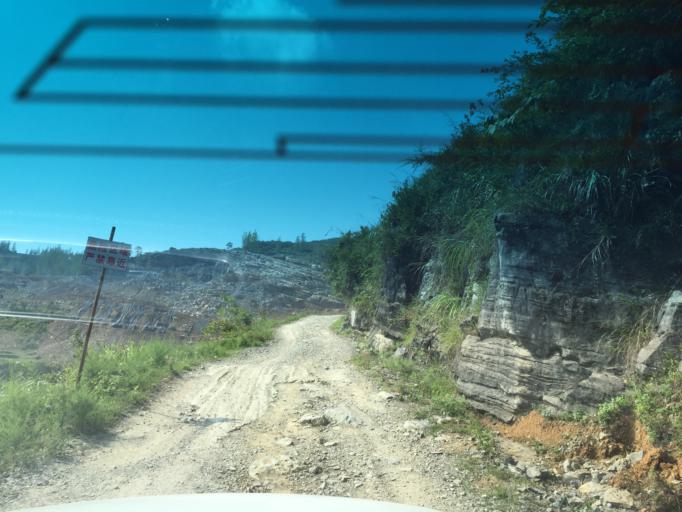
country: CN
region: Guizhou Sheng
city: Longquan
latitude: 28.2769
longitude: 108.0326
